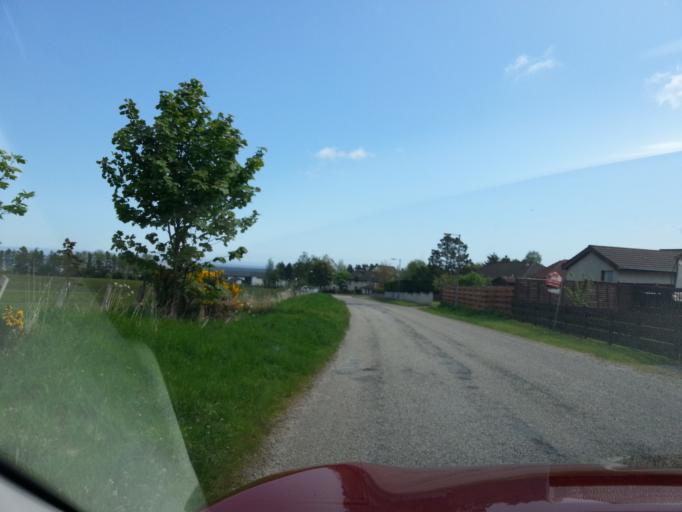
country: GB
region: Scotland
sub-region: Highland
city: Tain
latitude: 57.8072
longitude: -4.0726
